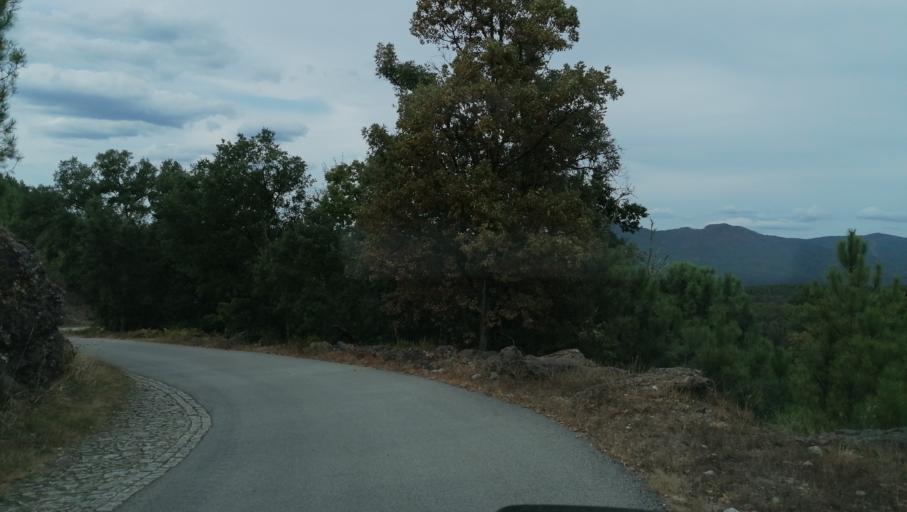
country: PT
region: Vila Real
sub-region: Vila Pouca de Aguiar
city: Vila Pouca de Aguiar
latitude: 41.5582
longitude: -7.7114
